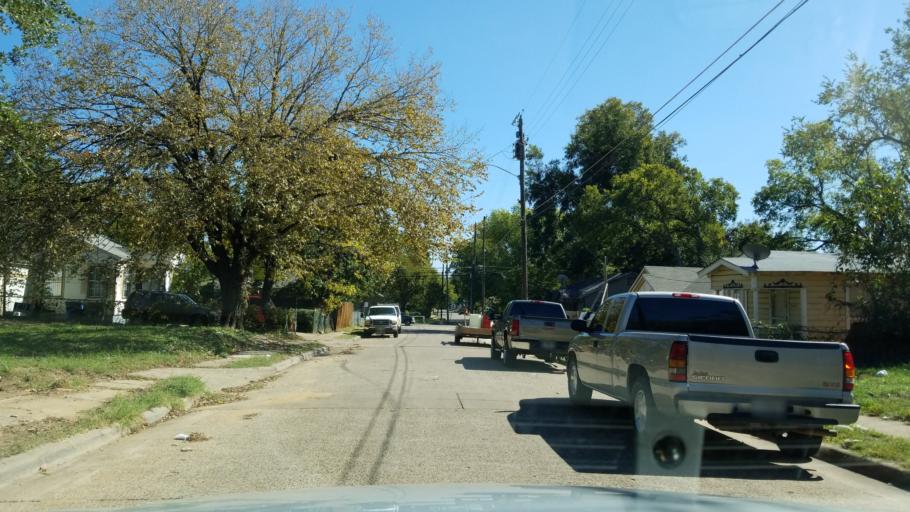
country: US
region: Texas
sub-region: Dallas County
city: Dallas
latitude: 32.7726
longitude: -96.7461
